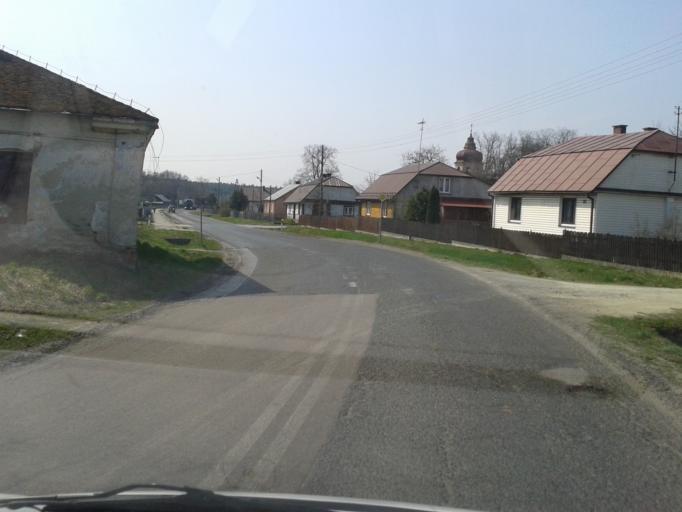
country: PL
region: Subcarpathian Voivodeship
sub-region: Powiat lubaczowski
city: Narol
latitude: 50.3138
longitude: 23.2444
